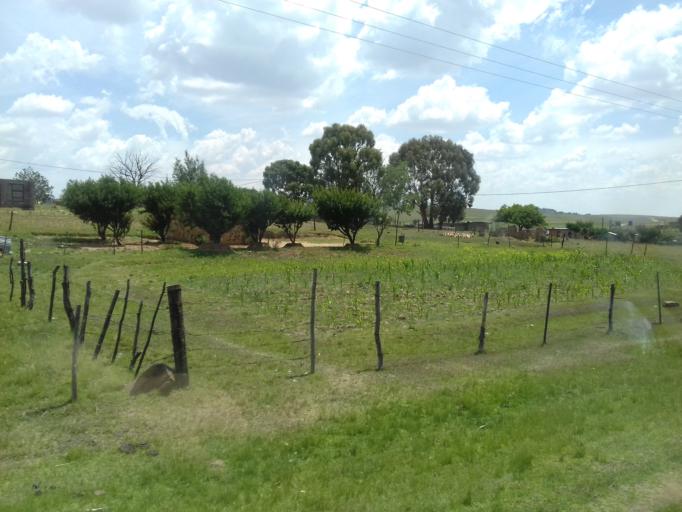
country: LS
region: Maseru
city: Nako
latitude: -29.5959
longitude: 27.5609
